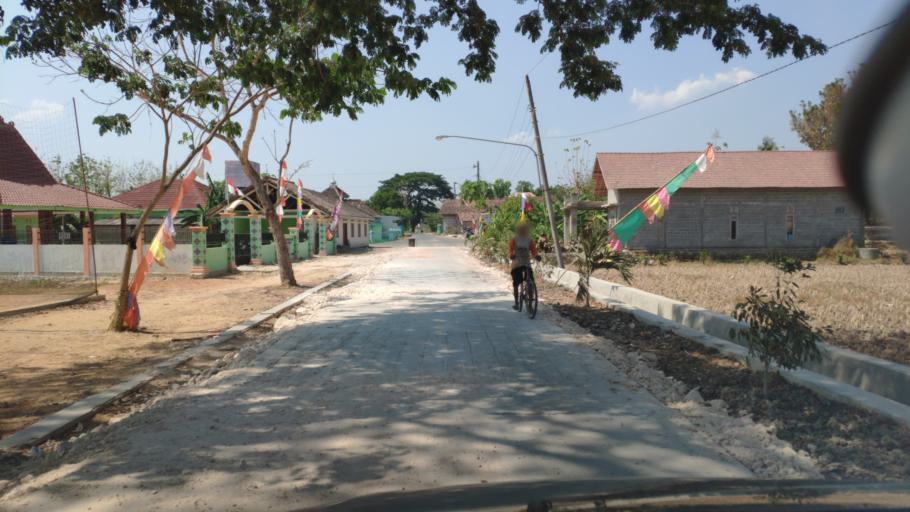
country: ID
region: Central Java
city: Geneng
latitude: -6.9120
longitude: 111.4112
